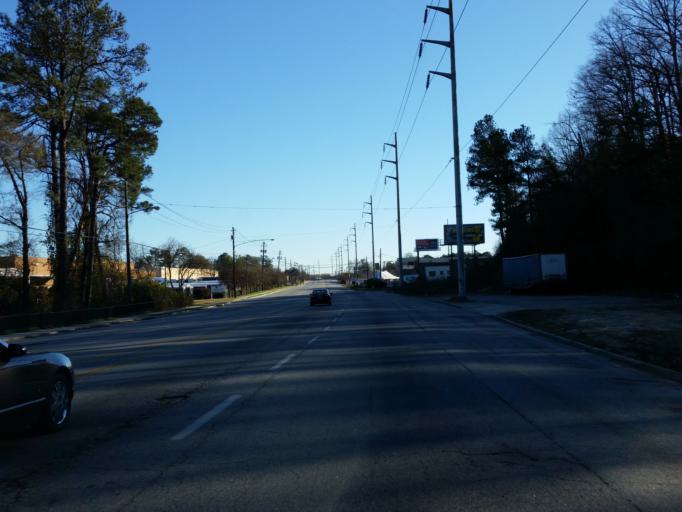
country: US
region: Georgia
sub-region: Cobb County
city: Vinings
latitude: 33.8085
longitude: -84.4383
